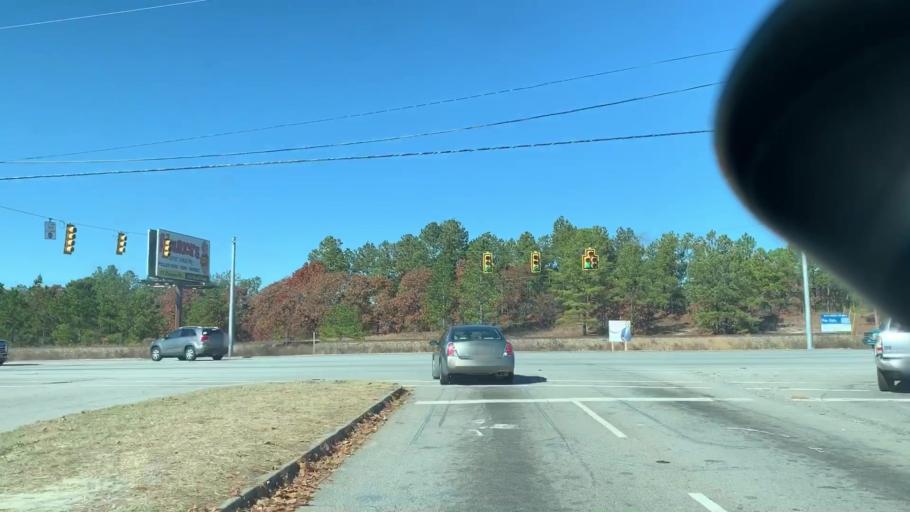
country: US
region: South Carolina
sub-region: Richland County
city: Woodfield
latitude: 34.1145
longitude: -80.8885
